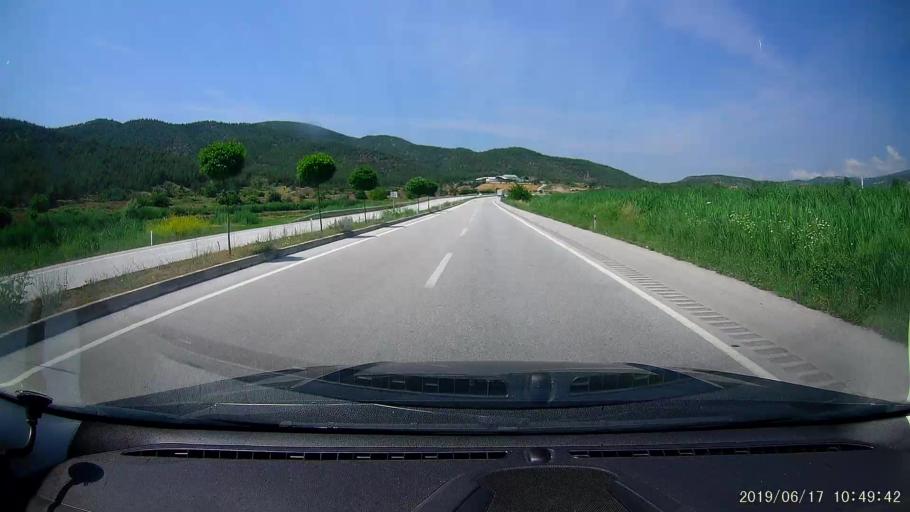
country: TR
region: Corum
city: Hacihamza
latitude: 41.1003
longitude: 34.4034
